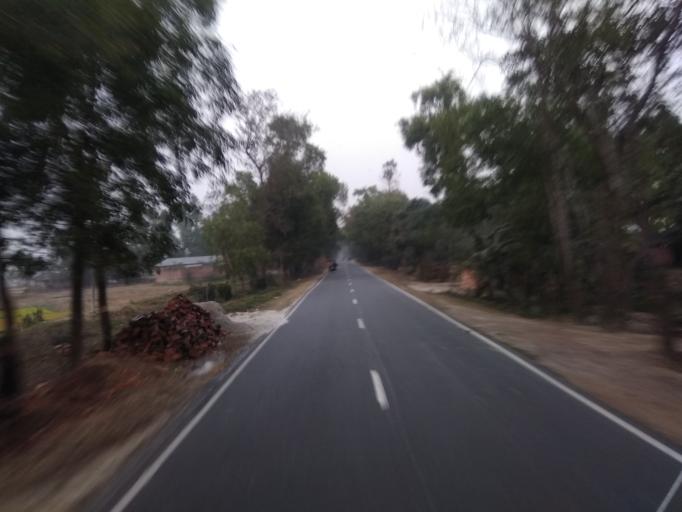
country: BD
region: Rajshahi
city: Bogra
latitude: 24.6527
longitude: 89.2601
